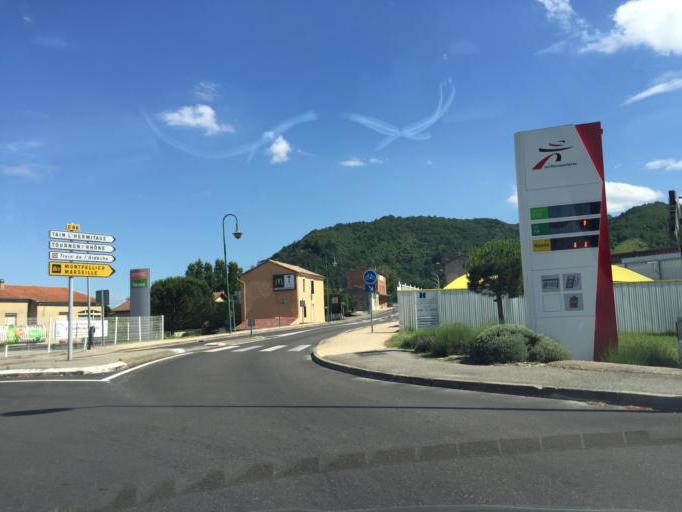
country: FR
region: Rhone-Alpes
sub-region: Departement de l'Ardeche
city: Saint-Jean-de-Muzols
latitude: 45.0764
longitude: 4.8156
